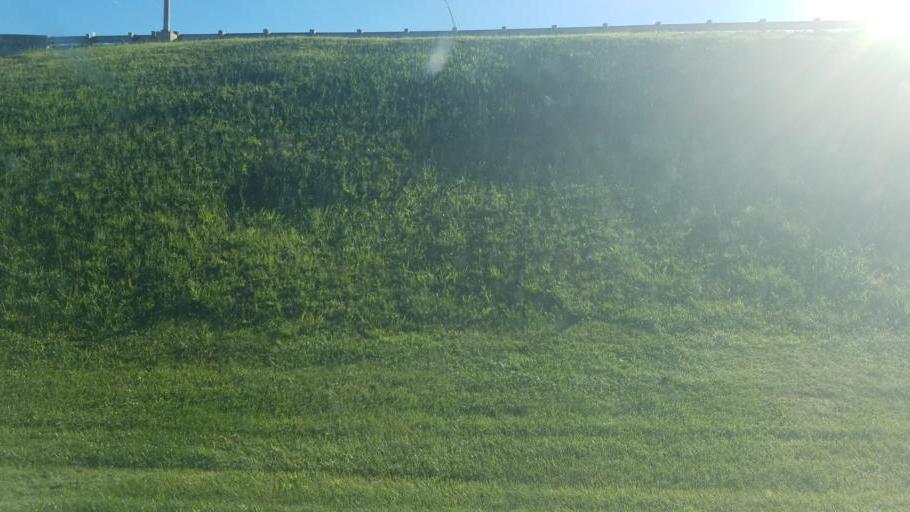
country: US
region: West Virginia
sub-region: Mason County
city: Point Pleasant
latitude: 38.8369
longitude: -82.1514
